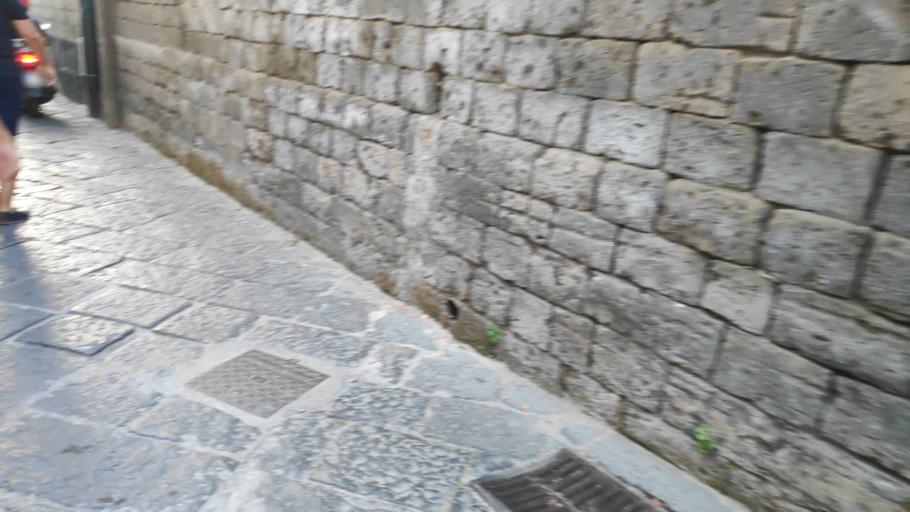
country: IT
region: Campania
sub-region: Provincia di Napoli
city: Sorrento
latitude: 40.6275
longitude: 14.3692
